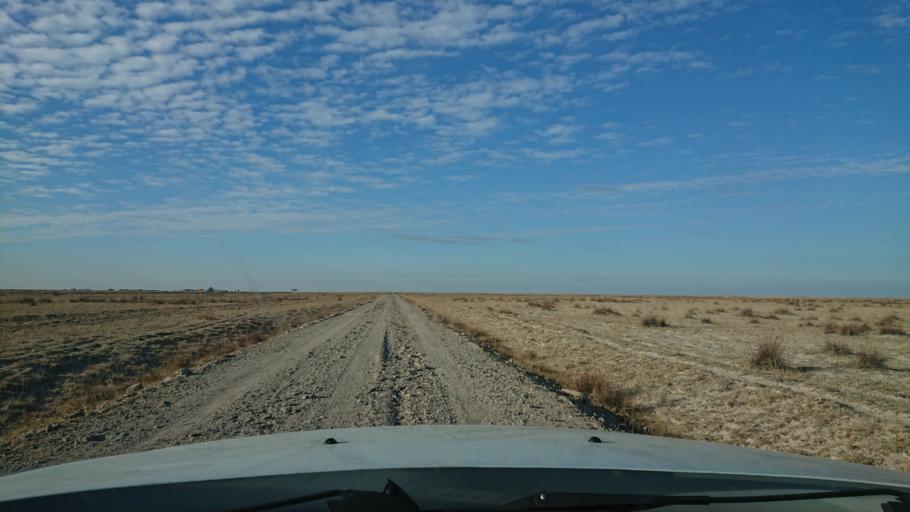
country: TR
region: Aksaray
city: Eskil
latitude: 38.5601
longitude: 33.3085
